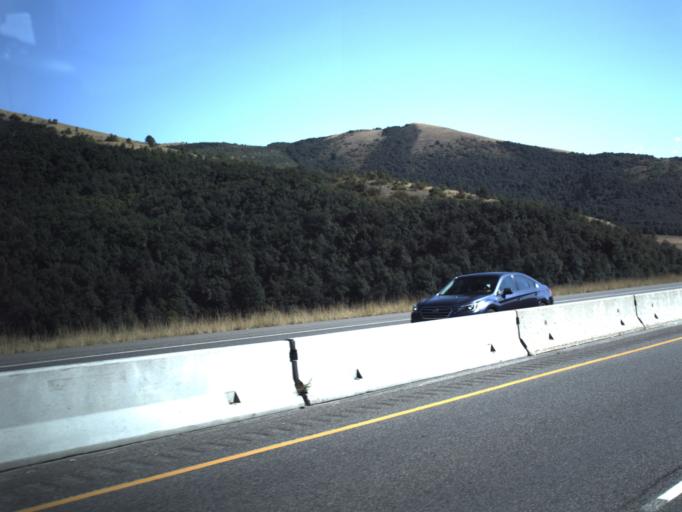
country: US
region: Utah
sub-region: Cache County
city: Wellsville
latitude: 41.5926
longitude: -111.9778
